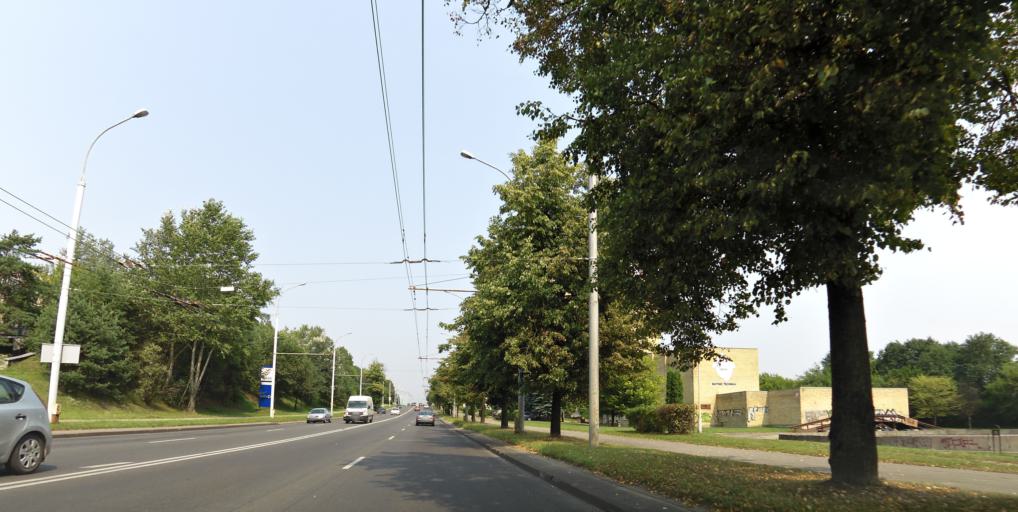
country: LT
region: Vilnius County
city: Rasos
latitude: 54.7070
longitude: 25.3047
